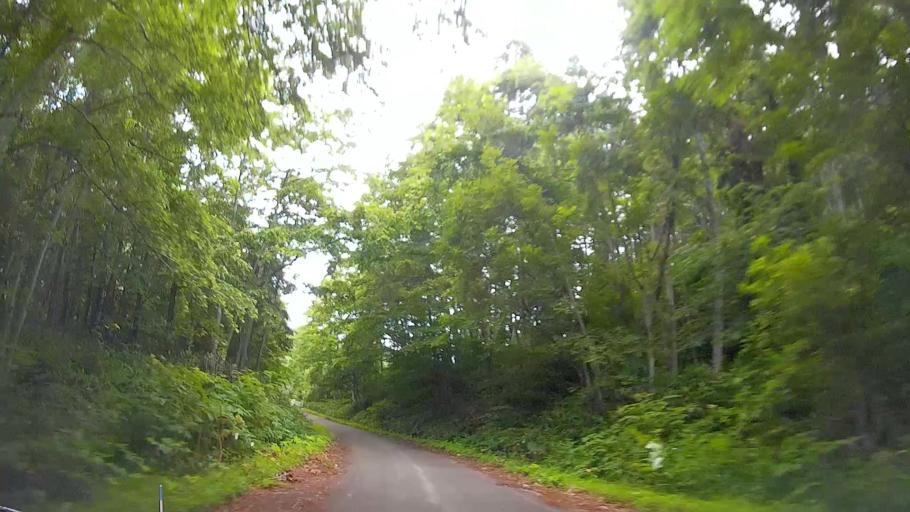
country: JP
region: Hokkaido
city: Nanae
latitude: 42.0551
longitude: 140.4971
